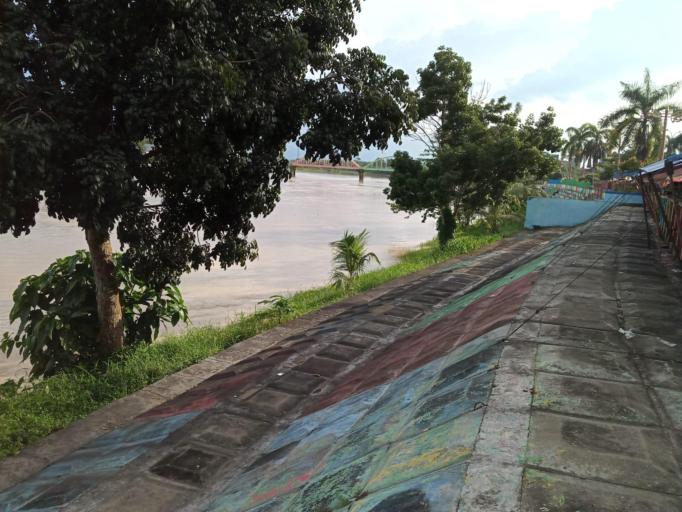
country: ID
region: Jambi
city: Sarolangun
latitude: -2.3035
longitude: 102.7250
